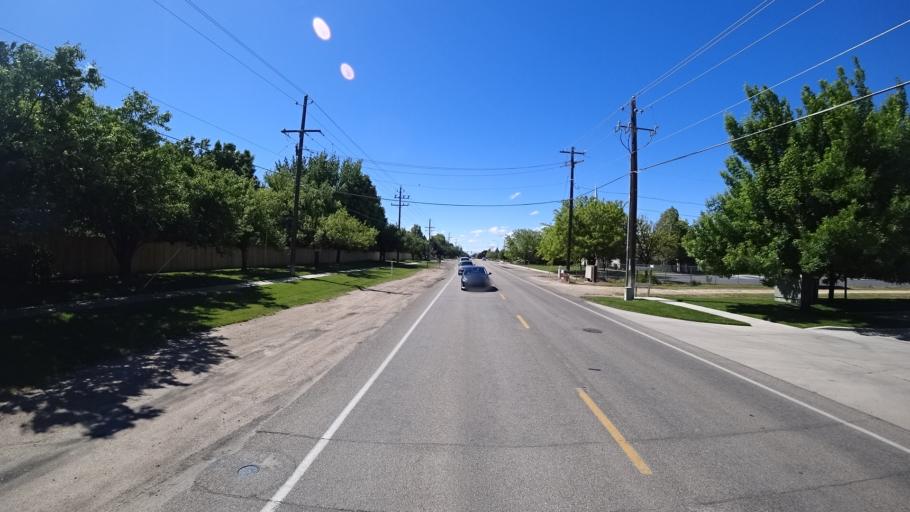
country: US
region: Idaho
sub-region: Ada County
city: Meridian
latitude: 43.6370
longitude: -116.3745
